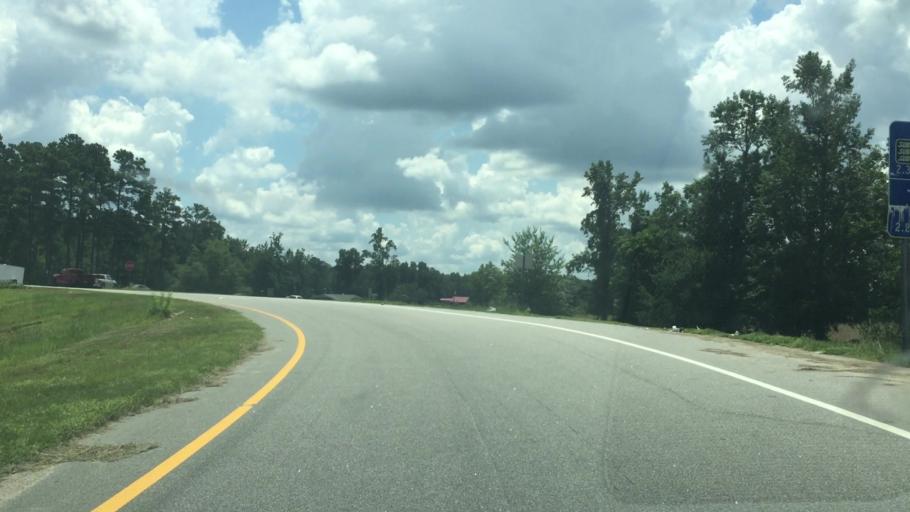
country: US
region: North Carolina
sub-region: Columbus County
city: Chadbourn
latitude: 34.3588
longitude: -78.8308
